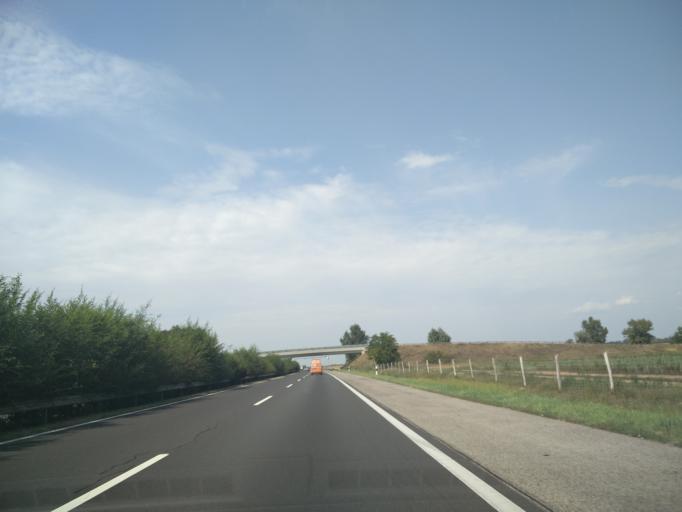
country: HU
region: Bacs-Kiskun
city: Lajosmizse
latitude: 47.0168
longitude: 19.5949
